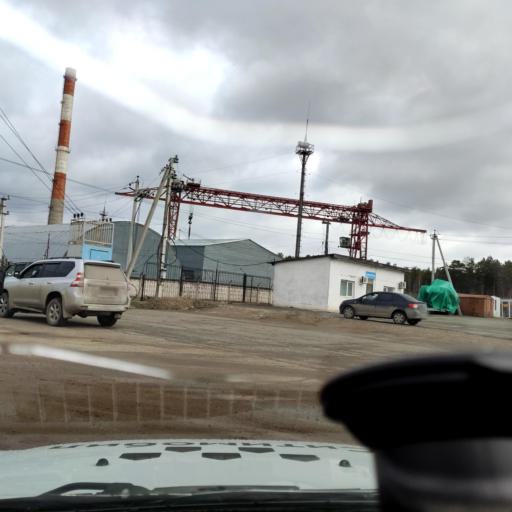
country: RU
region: Perm
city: Perm
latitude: 58.0384
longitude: 56.2068
